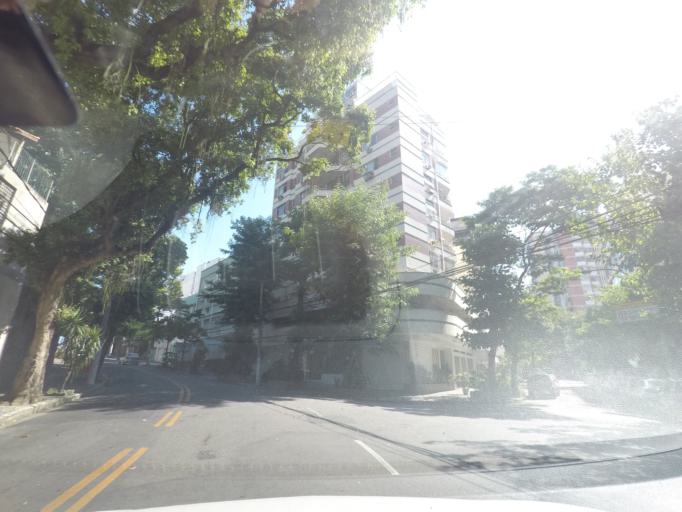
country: BR
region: Rio de Janeiro
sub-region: Niteroi
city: Niteroi
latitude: -22.9053
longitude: -43.1303
